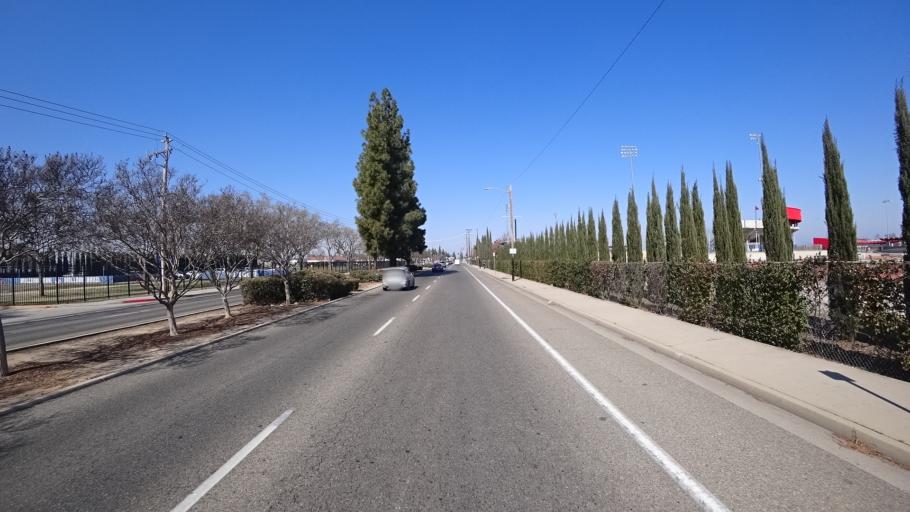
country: US
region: California
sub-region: Fresno County
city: Clovis
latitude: 36.8139
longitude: -119.7539
